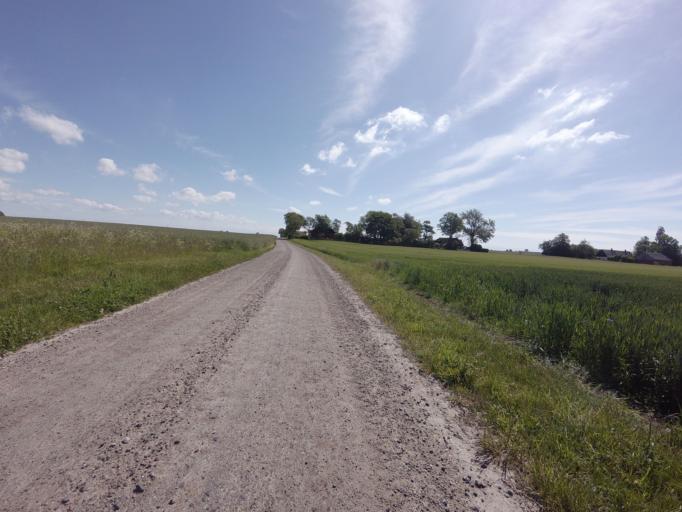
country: SE
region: Skane
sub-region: Trelleborgs Kommun
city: Skare
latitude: 55.4122
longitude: 13.0516
